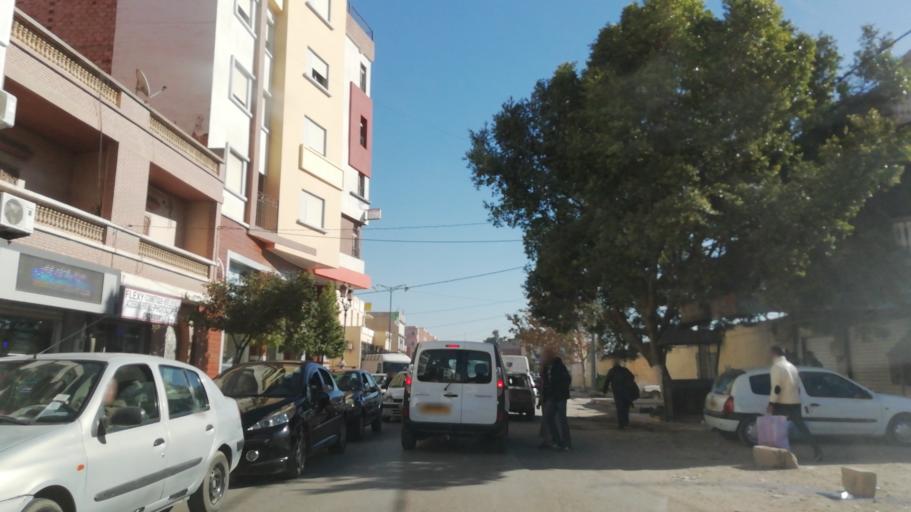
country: DZ
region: Tlemcen
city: Nedroma
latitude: 34.8455
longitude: -1.7246
